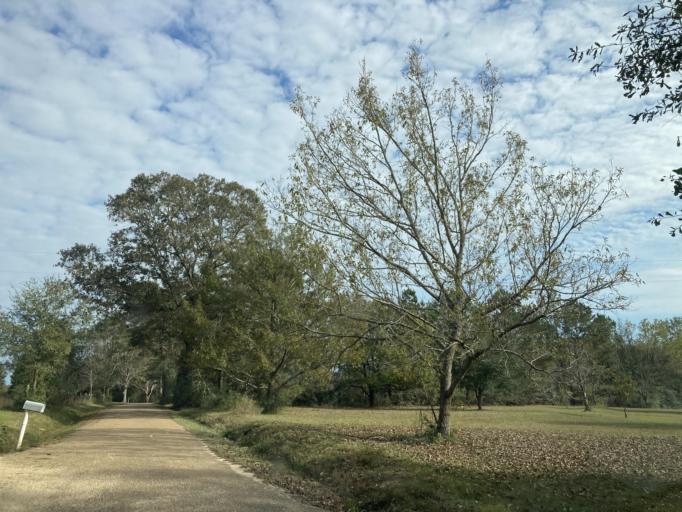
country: US
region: Mississippi
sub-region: Lamar County
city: Purvis
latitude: 31.2230
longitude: -89.3719
